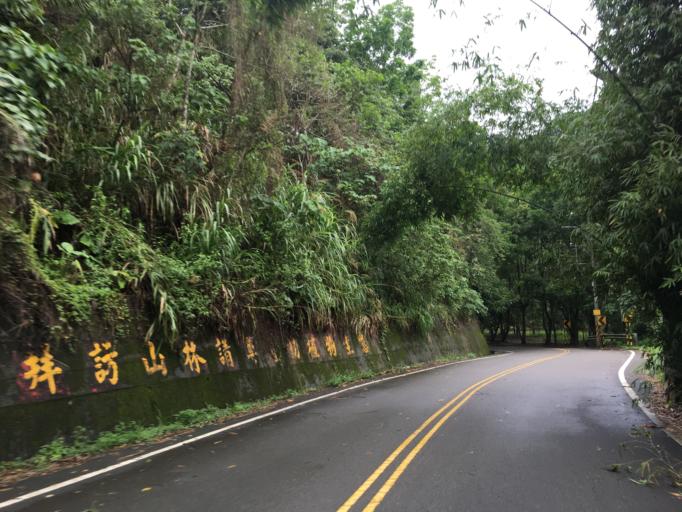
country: TW
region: Taiwan
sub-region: Taichung City
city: Taichung
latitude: 24.0663
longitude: 120.7423
